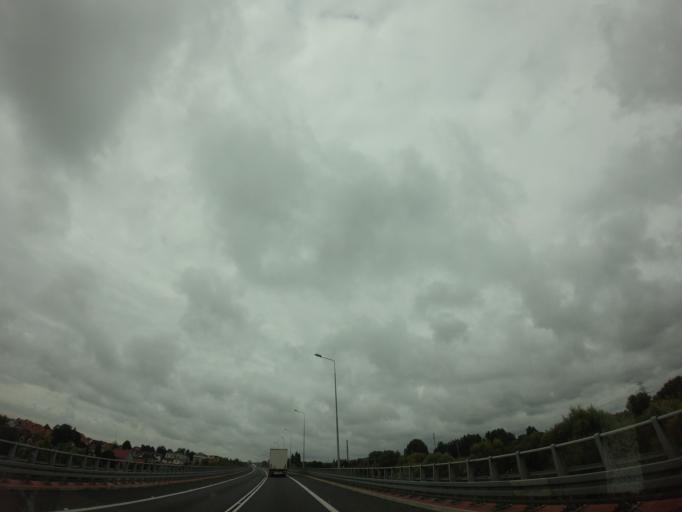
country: PL
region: West Pomeranian Voivodeship
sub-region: Powiat kamienski
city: Wolin
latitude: 53.8472
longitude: 14.6174
